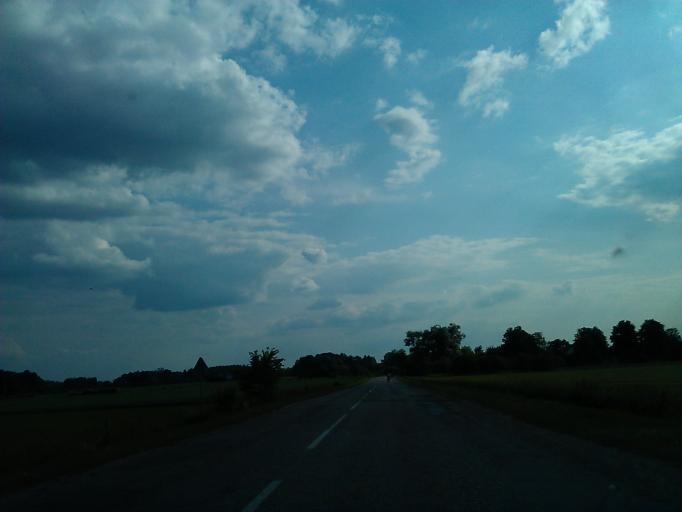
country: LV
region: Aizpute
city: Aizpute
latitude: 56.7226
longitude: 21.6432
